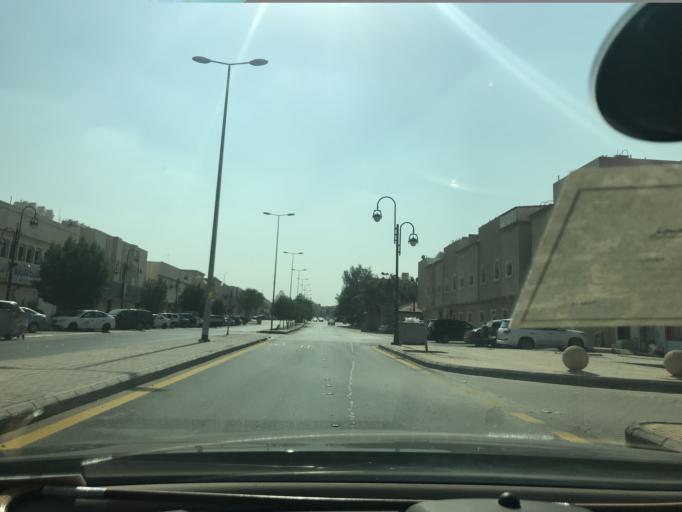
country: SA
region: Ar Riyad
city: Riyadh
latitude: 24.7403
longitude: 46.7672
